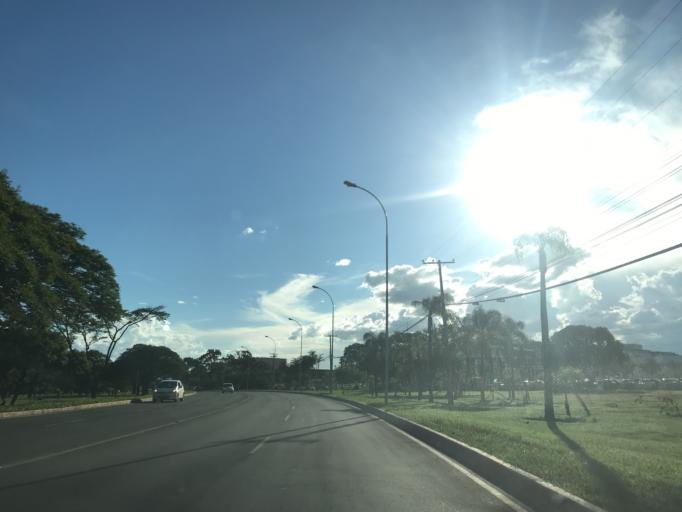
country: BR
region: Federal District
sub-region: Brasilia
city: Brasilia
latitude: -15.7894
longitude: -47.9075
